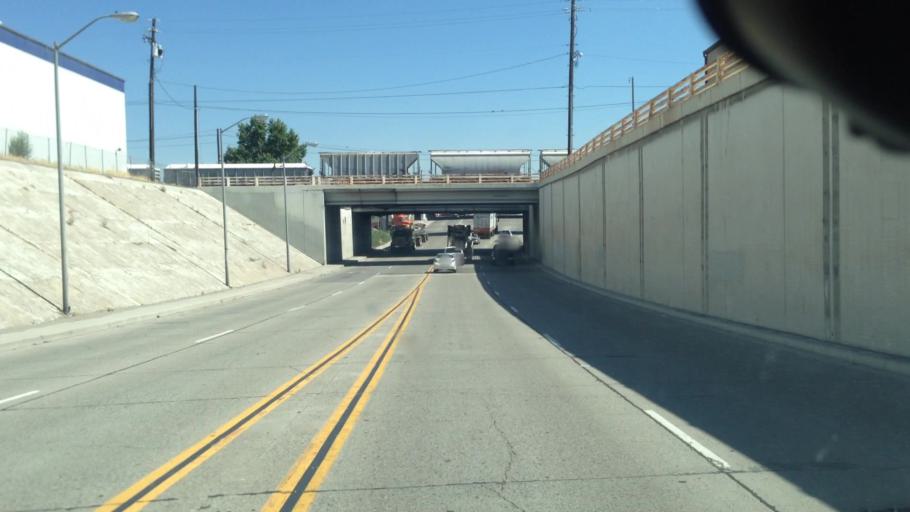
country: US
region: Nevada
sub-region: Washoe County
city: Sparks
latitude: 39.5318
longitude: -119.7660
